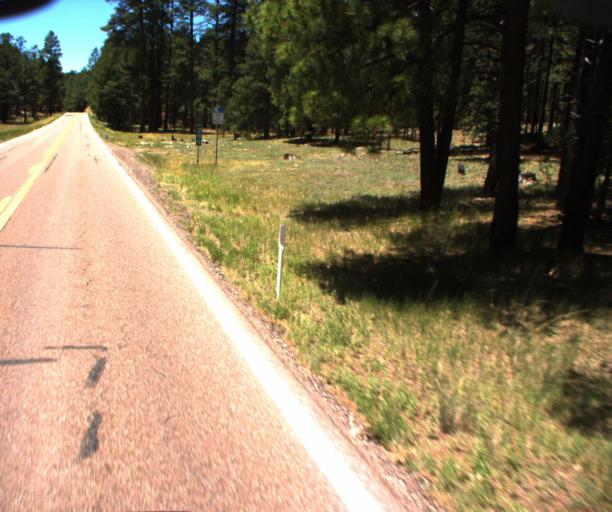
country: US
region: Arizona
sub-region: Gila County
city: Pine
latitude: 34.5373
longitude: -111.3335
